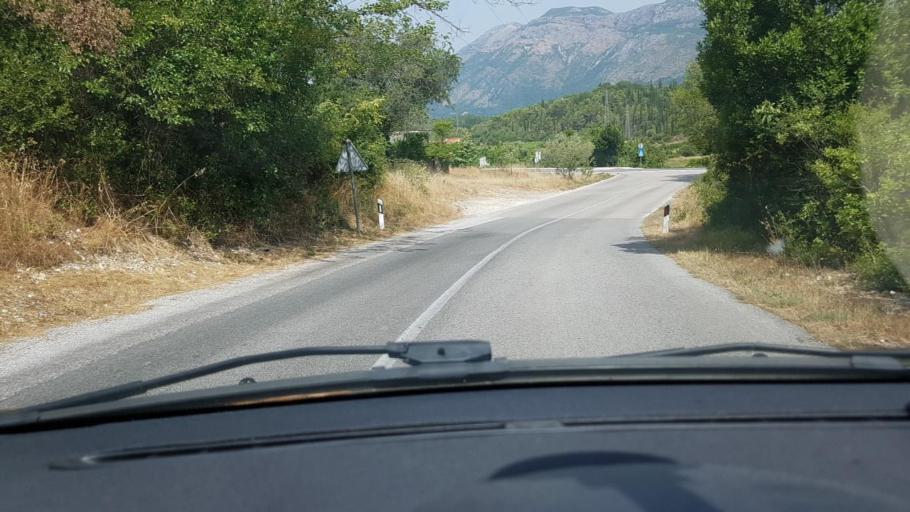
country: ME
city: Igalo
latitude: 42.5052
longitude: 18.4029
